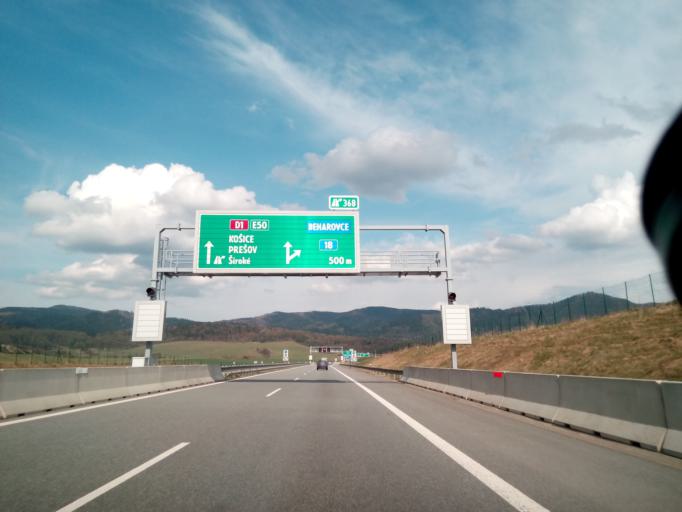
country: SK
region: Presovsky
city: Spisske Podhradie
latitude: 49.0079
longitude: 20.7994
